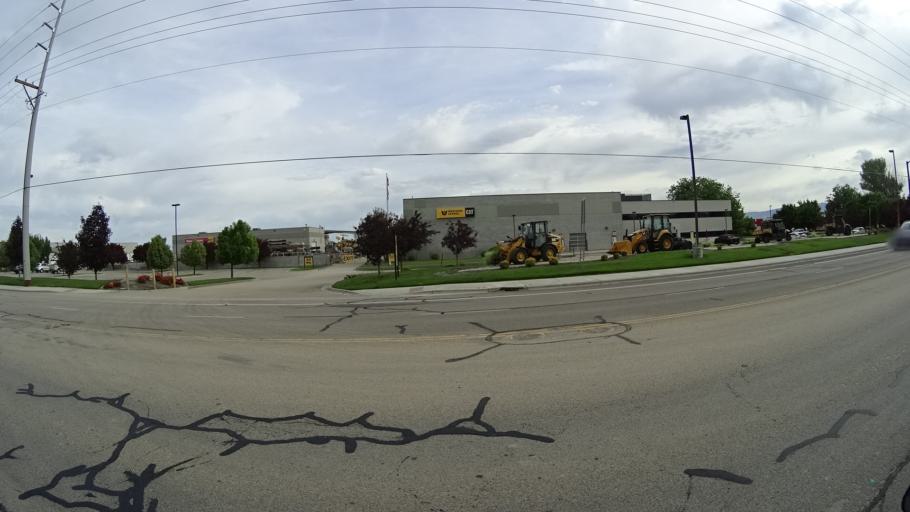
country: US
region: Idaho
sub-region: Ada County
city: Meridian
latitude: 43.5900
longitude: -116.3863
